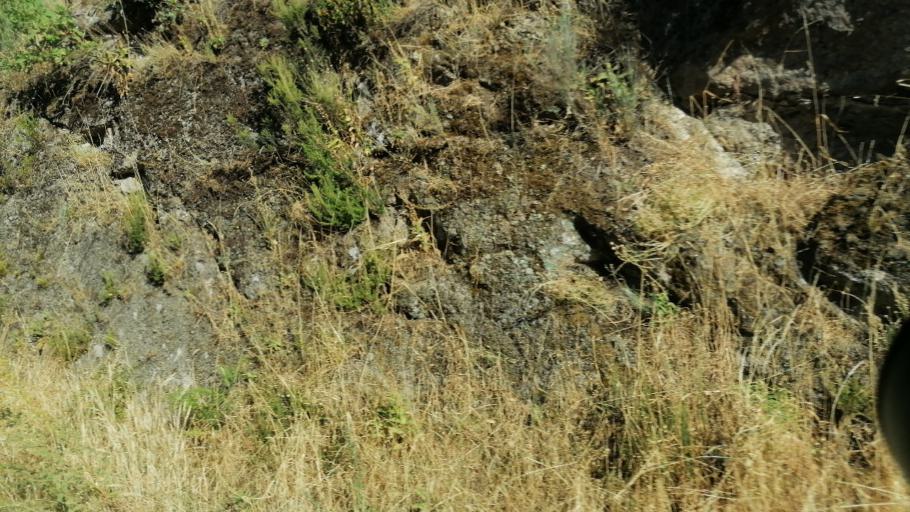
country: PT
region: Vila Real
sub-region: Murca
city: Murca
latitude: 41.4007
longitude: -7.4816
